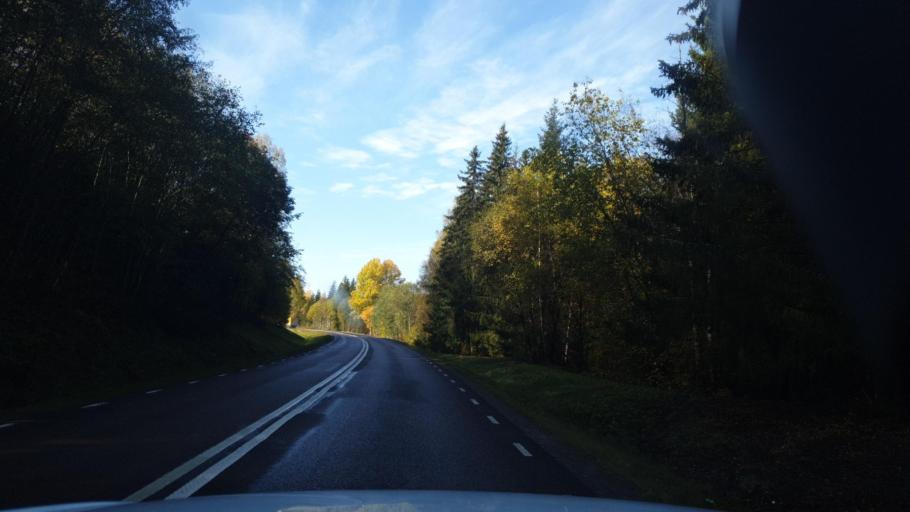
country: SE
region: Vaermland
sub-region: Eda Kommun
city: Amotfors
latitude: 59.6808
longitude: 12.4018
